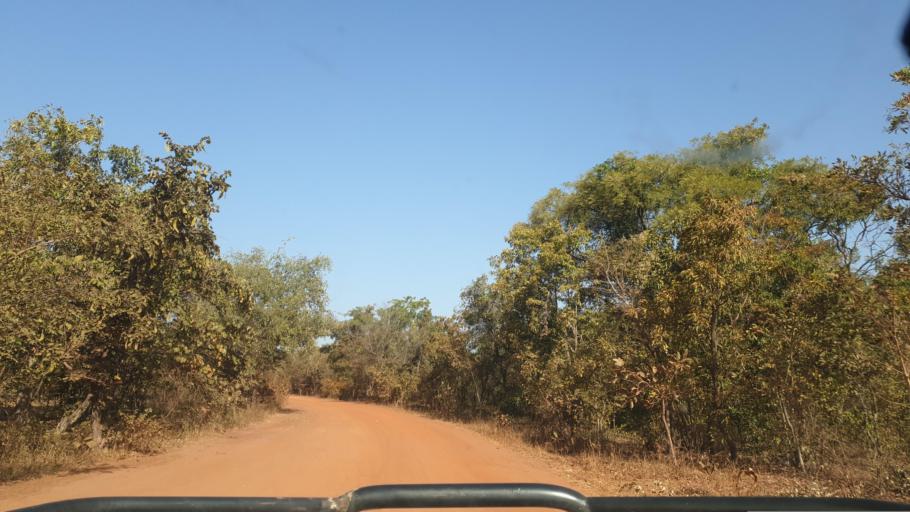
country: ML
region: Sikasso
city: Bougouni
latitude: 11.7836
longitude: -6.9087
